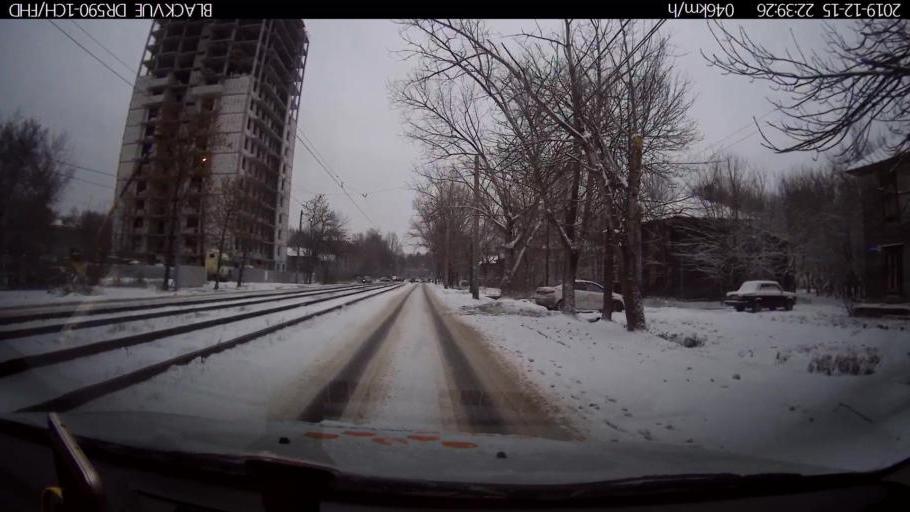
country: RU
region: Nizjnij Novgorod
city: Gorbatovka
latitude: 56.3390
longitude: 43.8403
